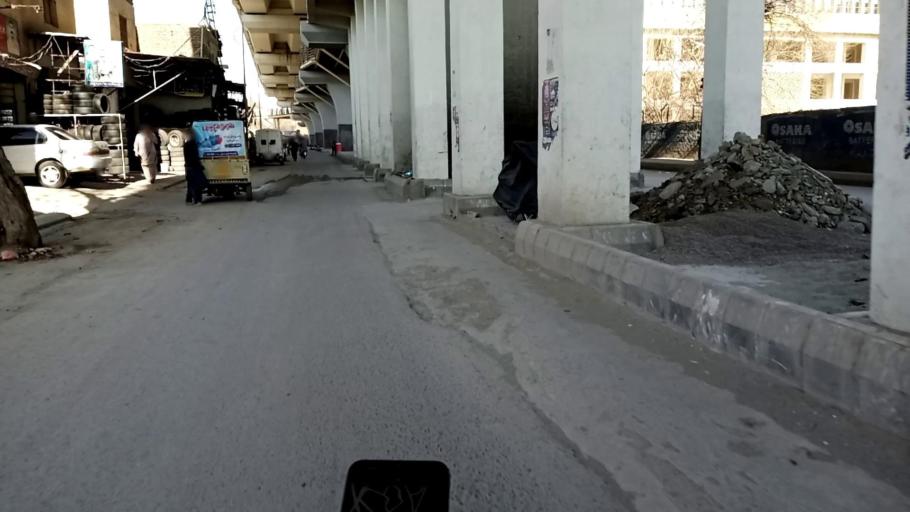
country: PK
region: Khyber Pakhtunkhwa
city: Peshawar
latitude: 34.0053
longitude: 71.5568
